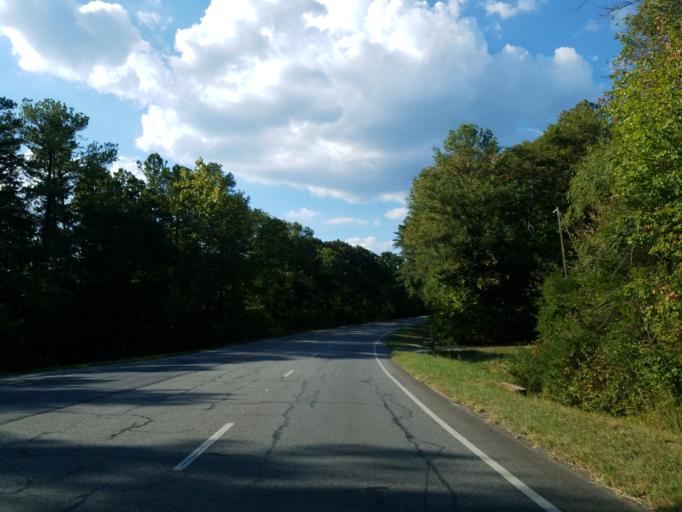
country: US
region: Georgia
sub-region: Bartow County
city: Rydal
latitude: 34.4750
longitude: -84.7058
